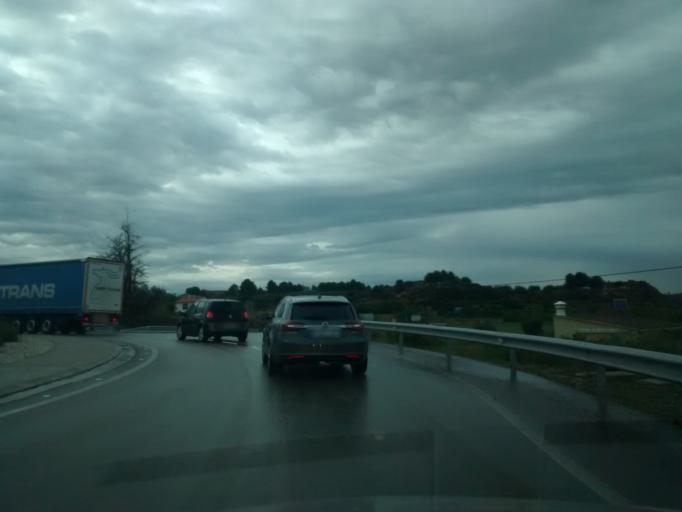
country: ES
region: Aragon
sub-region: Provincia de Zaragoza
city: Maella
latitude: 41.1293
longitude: 0.1301
